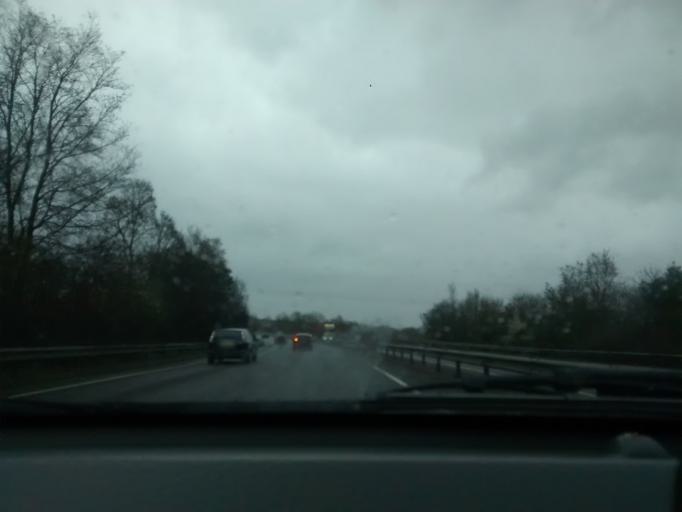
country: GB
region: England
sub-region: Suffolk
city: Stowmarket
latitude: 52.1986
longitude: 0.9888
